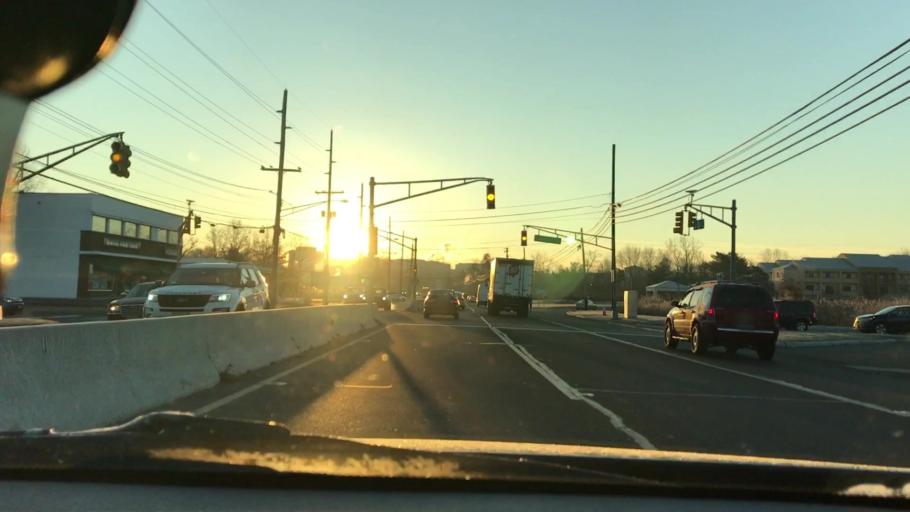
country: US
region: New Jersey
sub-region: Morris County
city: Florham Park
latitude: 40.8167
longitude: -74.4017
